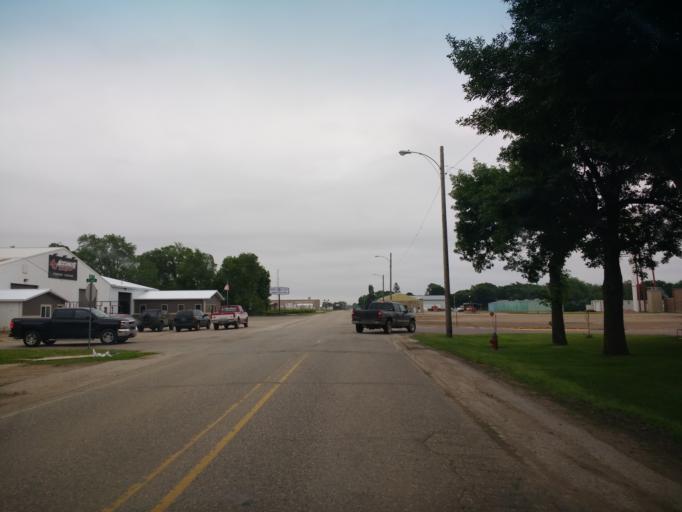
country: US
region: Iowa
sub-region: Dickinson County
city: Milford
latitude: 43.3279
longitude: -95.1485
